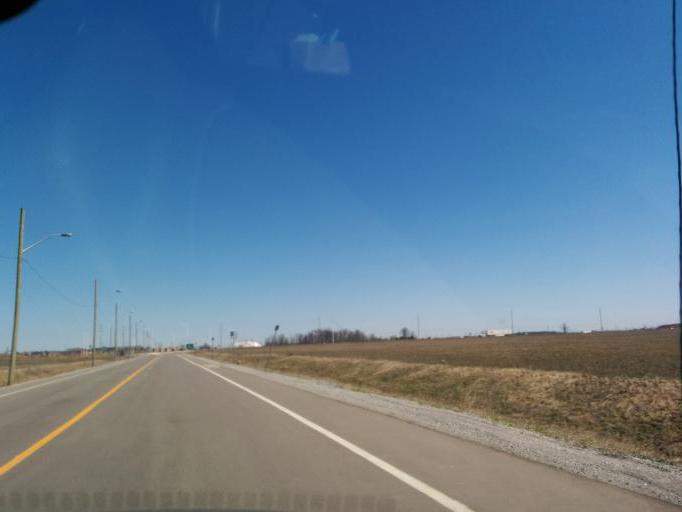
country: CA
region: Ontario
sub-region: Halton
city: Milton
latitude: 43.4739
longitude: -79.8728
